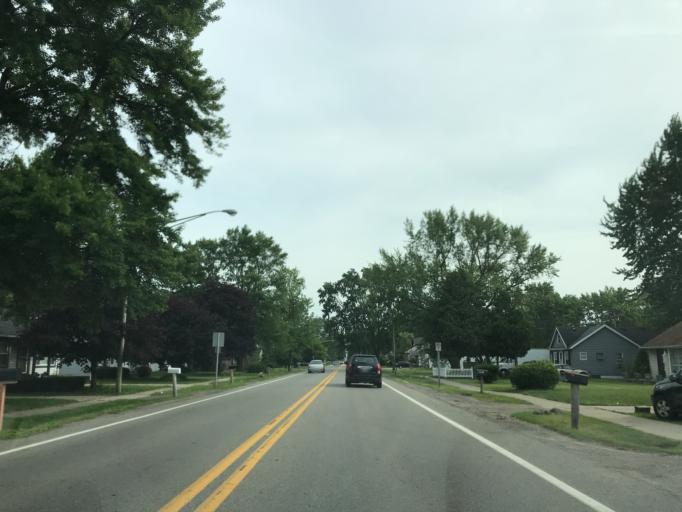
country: US
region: Michigan
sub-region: Wayne County
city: Redford
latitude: 42.4376
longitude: -83.3167
